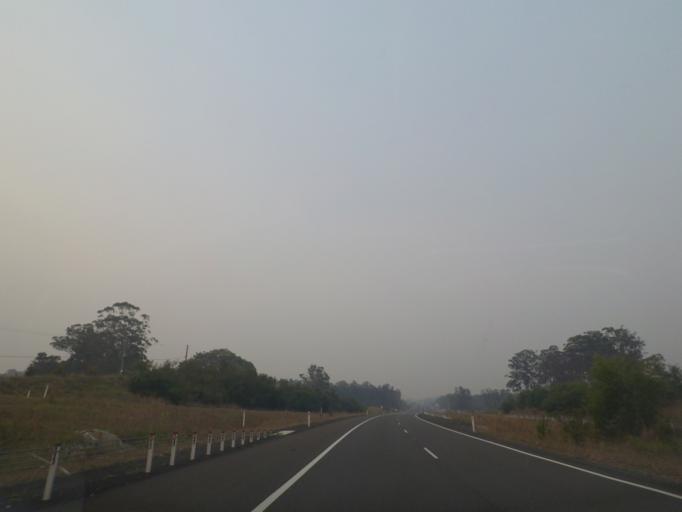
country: AU
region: New South Wales
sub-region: Nambucca Shire
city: Macksville
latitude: -30.7313
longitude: 152.9216
